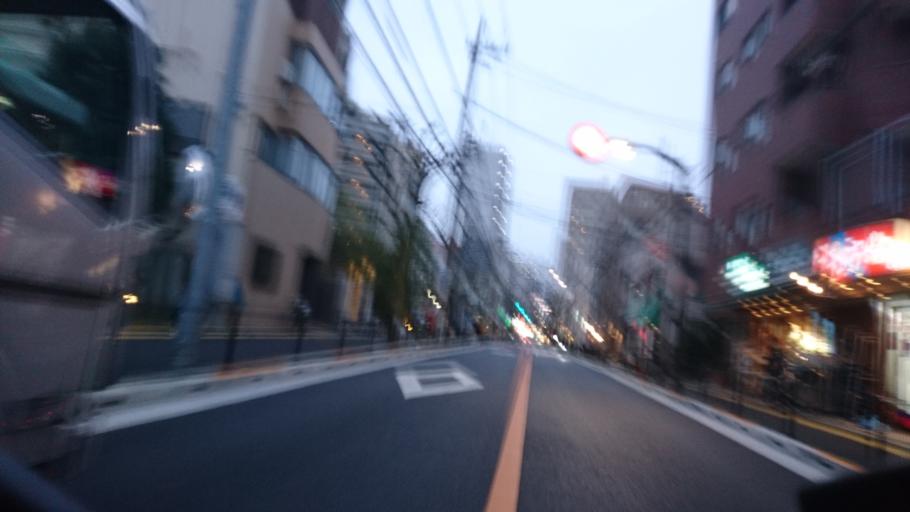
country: JP
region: Kanagawa
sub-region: Kawasaki-shi
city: Kawasaki
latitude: 35.6089
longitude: 139.7379
